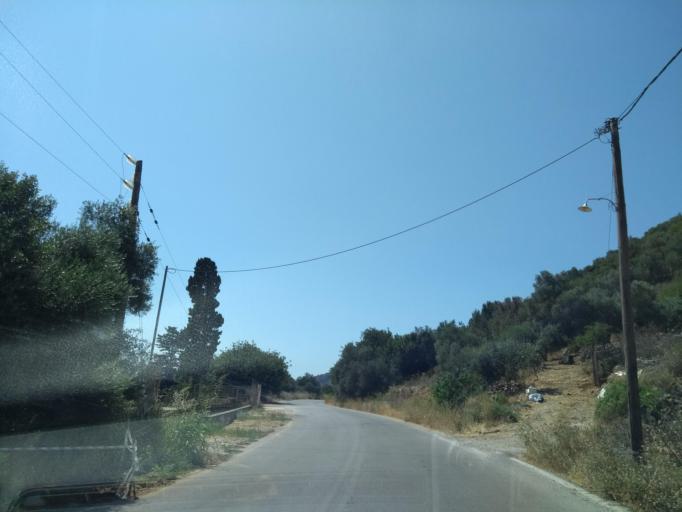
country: GR
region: Crete
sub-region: Nomos Chanias
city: Georgioupolis
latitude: 35.3800
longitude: 24.2426
